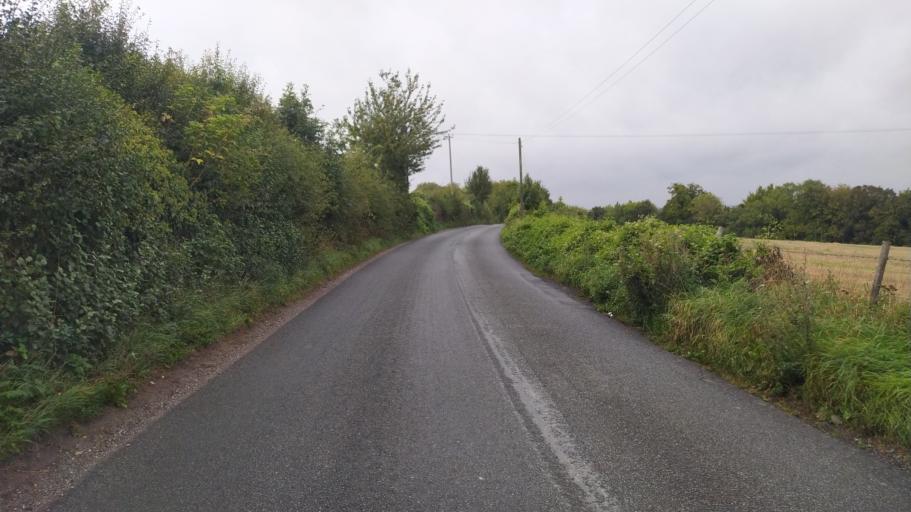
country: GB
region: England
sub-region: Wiltshire
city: Allington
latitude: 51.1255
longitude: -1.7314
